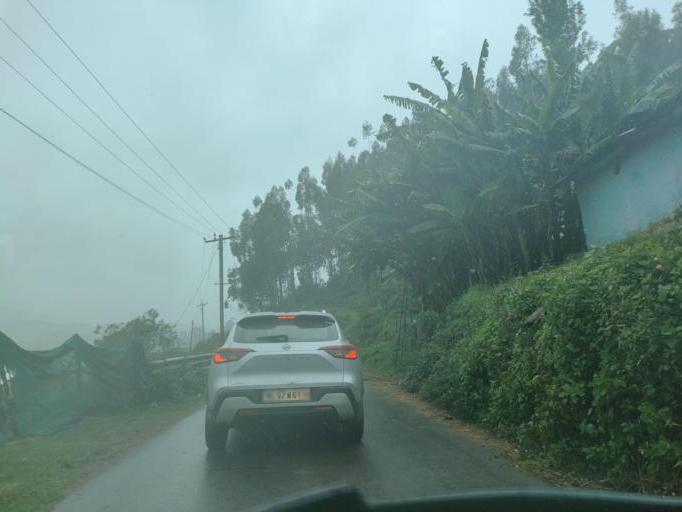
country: IN
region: Tamil Nadu
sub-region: Dindigul
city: Kodaikanal
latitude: 10.2365
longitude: 77.3497
